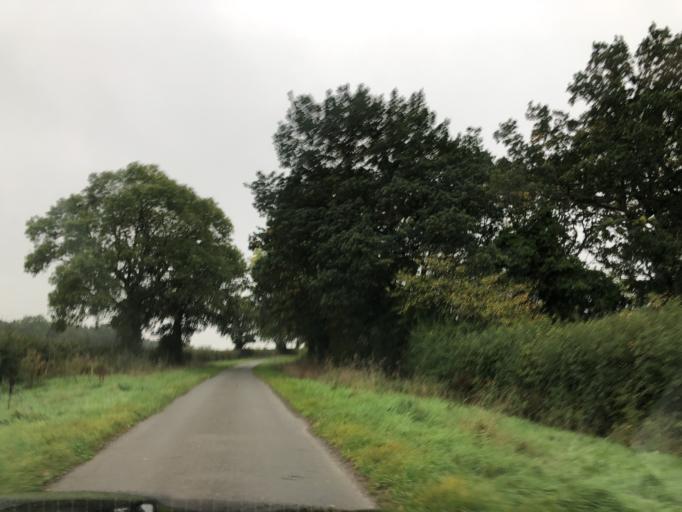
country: GB
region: England
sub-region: Warwickshire
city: Wroxall
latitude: 52.3211
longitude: -1.6559
